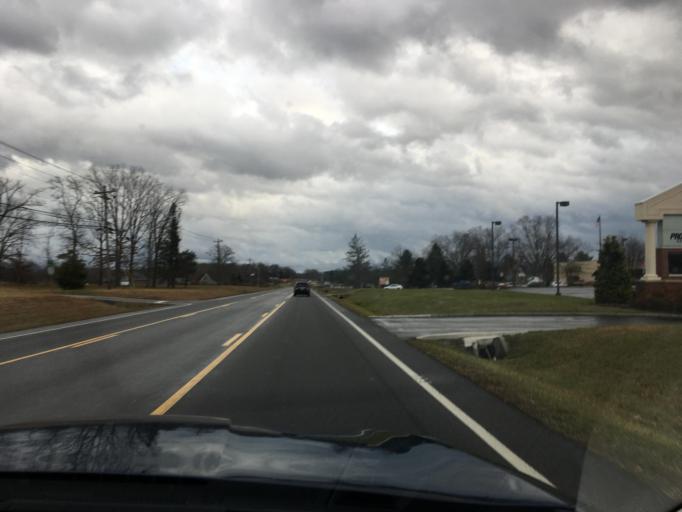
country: US
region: Tennessee
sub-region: Cumberland County
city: Crossville
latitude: 35.9282
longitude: -85.0078
